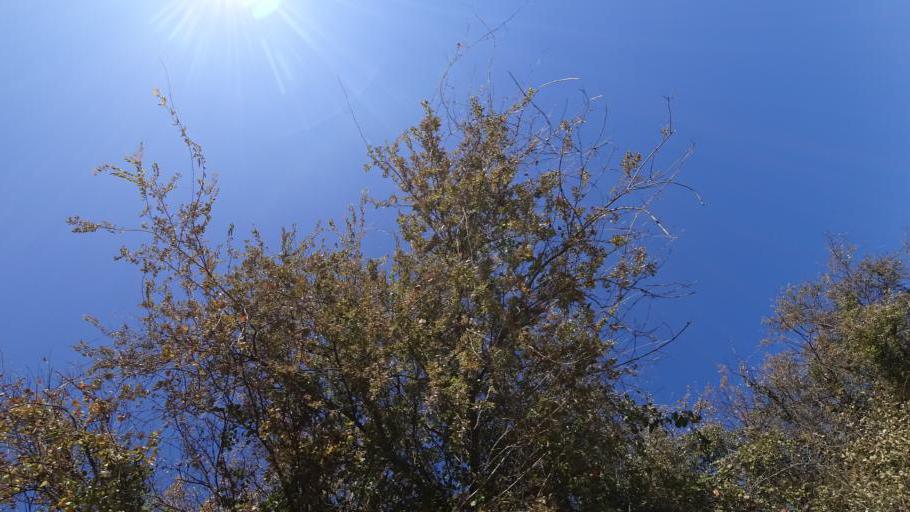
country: US
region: Texas
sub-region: Denton County
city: Lewisville
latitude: 33.0374
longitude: -96.9401
